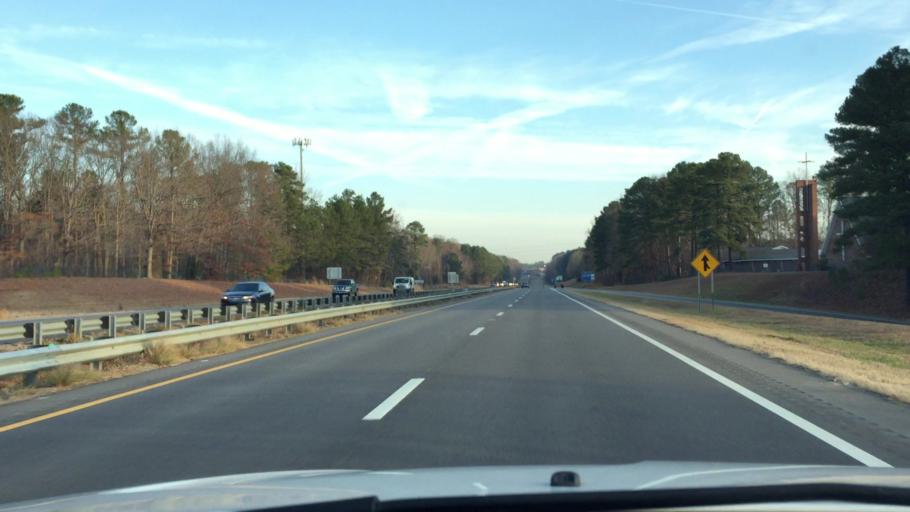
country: US
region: North Carolina
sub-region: Lee County
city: Sanford
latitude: 35.4698
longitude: -79.2025
